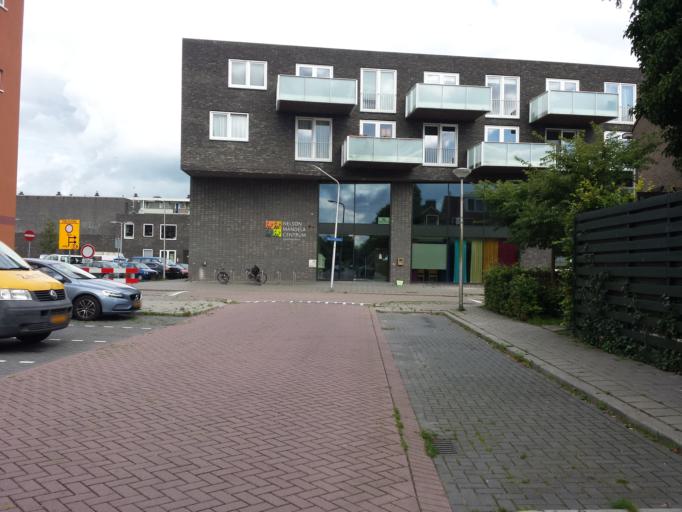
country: NL
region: South Holland
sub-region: Gemeente Gouda
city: Gouda
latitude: 52.0130
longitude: 4.7274
